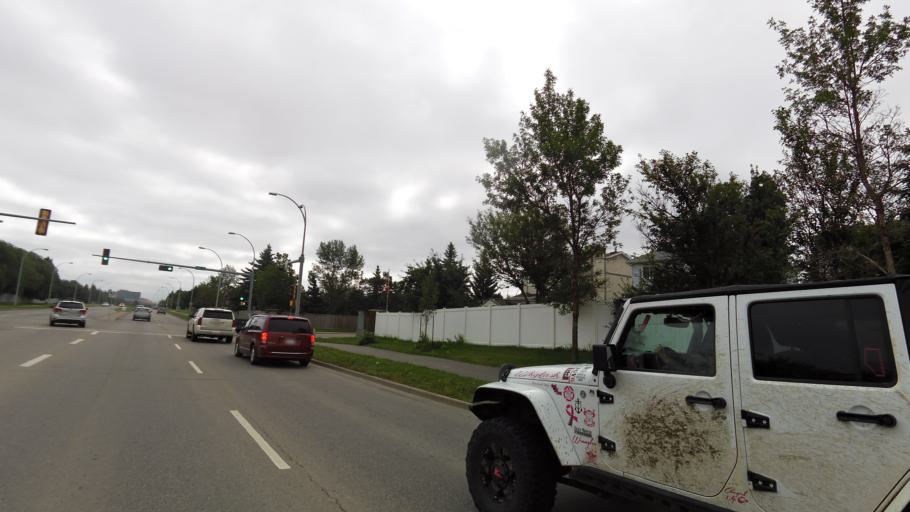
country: CA
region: Alberta
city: St. Albert
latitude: 53.5213
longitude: -113.6499
